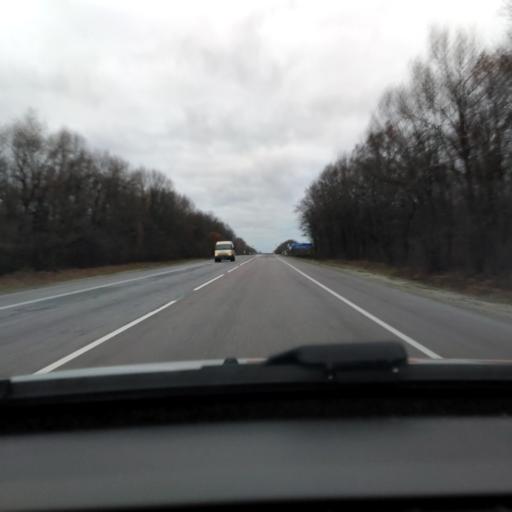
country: RU
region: Lipetsk
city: Khlevnoye
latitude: 52.3054
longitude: 39.1668
